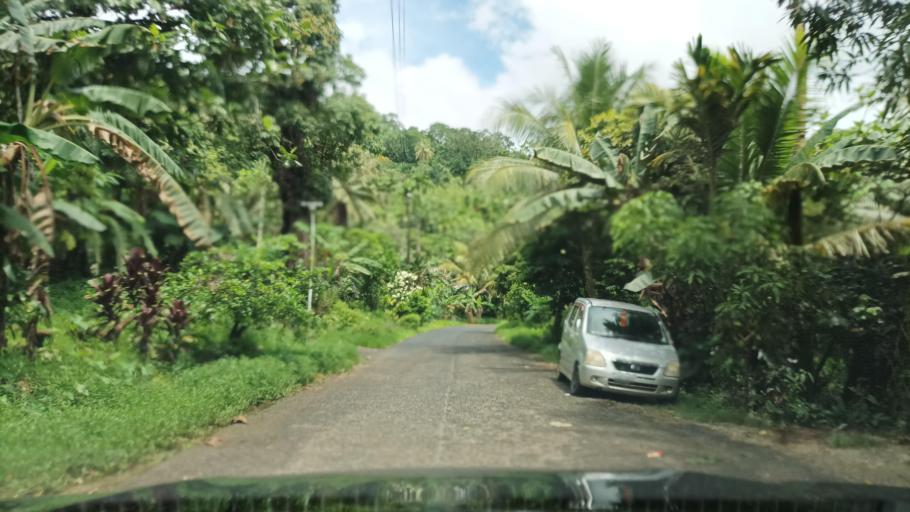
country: FM
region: Pohnpei
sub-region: Kolonia Municipality
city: Kolonia
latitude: 6.9571
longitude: 158.2262
